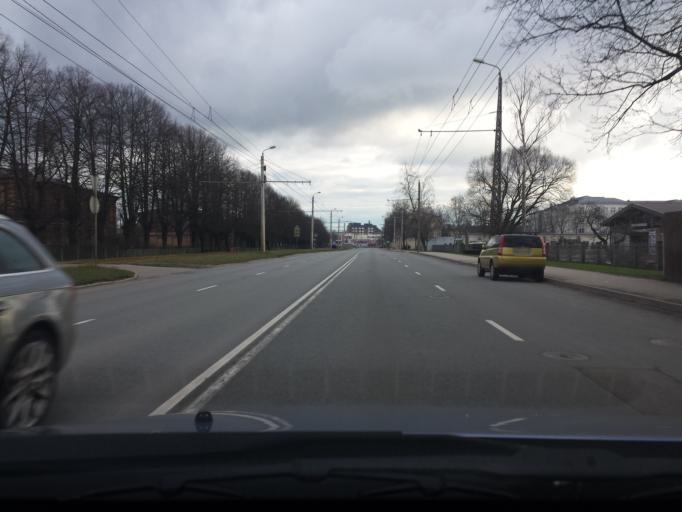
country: LV
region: Riga
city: Riga
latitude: 56.9724
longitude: 24.1099
